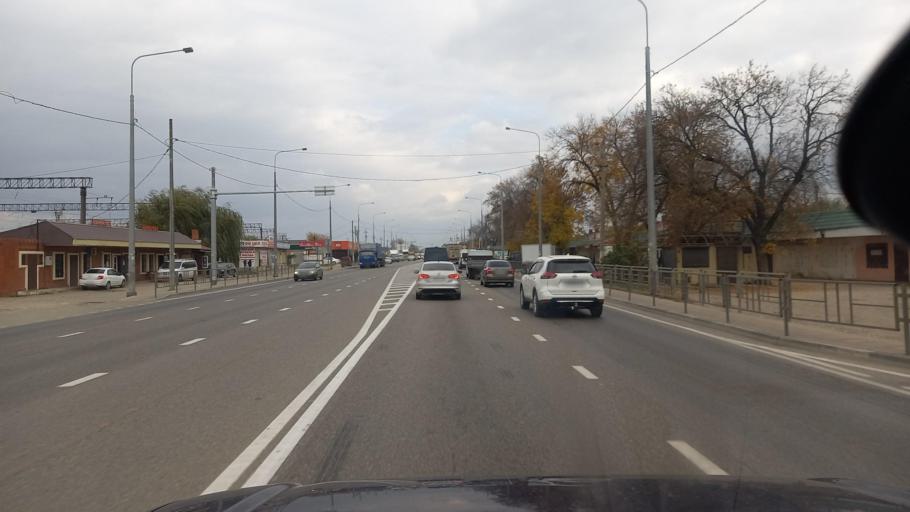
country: RU
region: Adygeya
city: Enem
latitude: 44.9256
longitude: 38.9049
